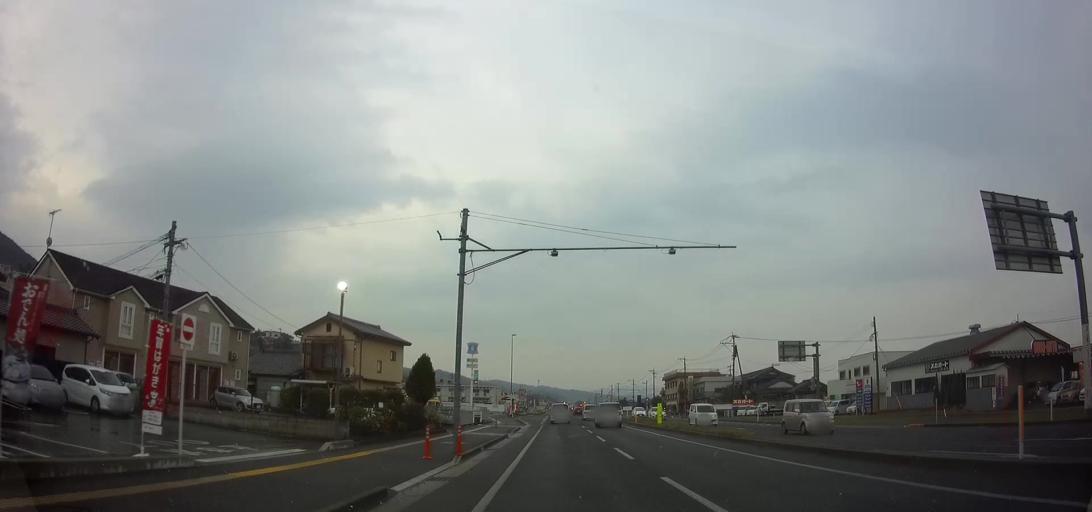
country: JP
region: Nagasaki
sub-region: Isahaya-shi
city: Isahaya
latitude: 32.8359
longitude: 130.0937
